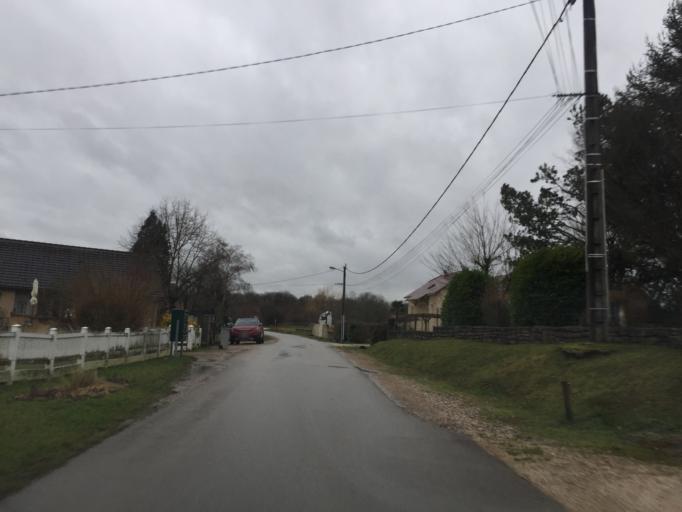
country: FR
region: Franche-Comte
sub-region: Departement du Jura
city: Champvans
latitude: 47.1465
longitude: 5.4546
